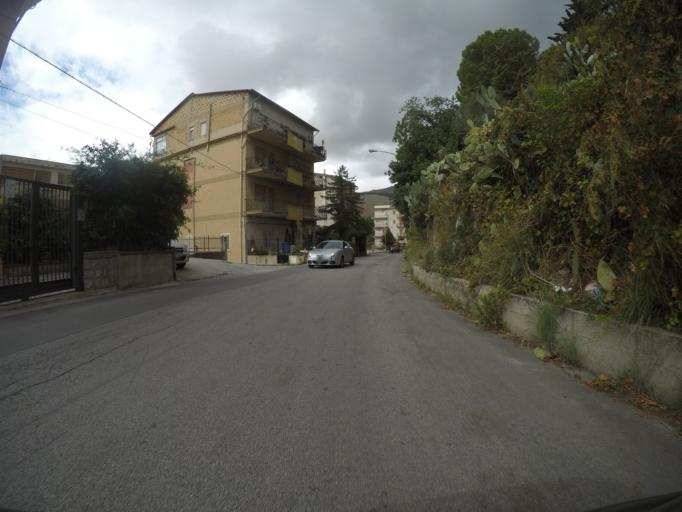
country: IT
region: Sicily
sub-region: Palermo
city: Montelepre
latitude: 38.0925
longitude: 13.1719
